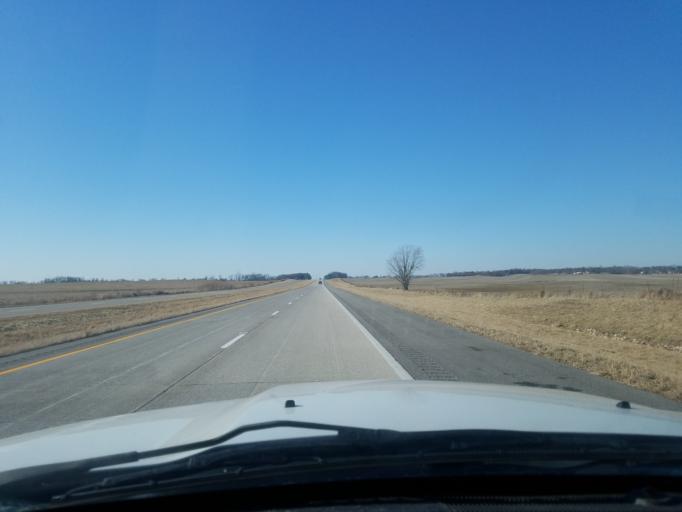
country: US
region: Kentucky
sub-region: Henderson County
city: Henderson
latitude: 37.8012
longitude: -87.5168
